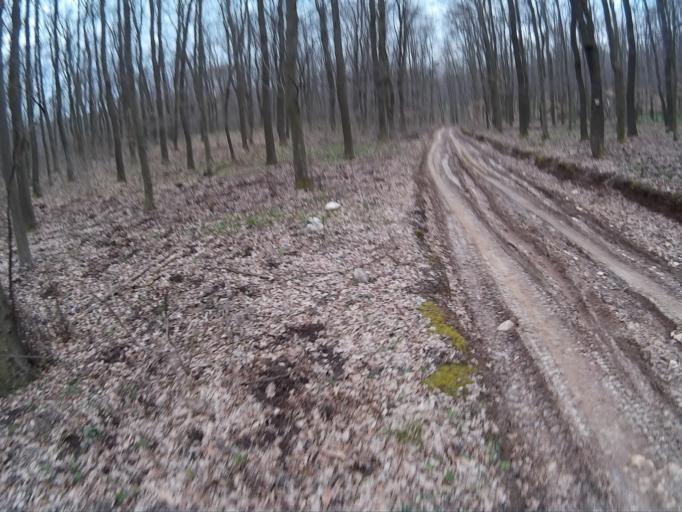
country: HU
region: Veszprem
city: Zirc
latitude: 47.1833
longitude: 17.8892
